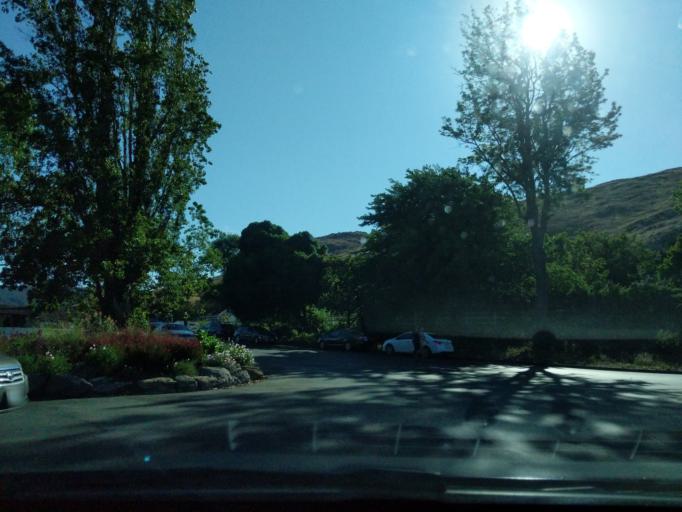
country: US
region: California
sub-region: San Luis Obispo County
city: San Luis Obispo
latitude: 35.2667
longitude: -120.6747
